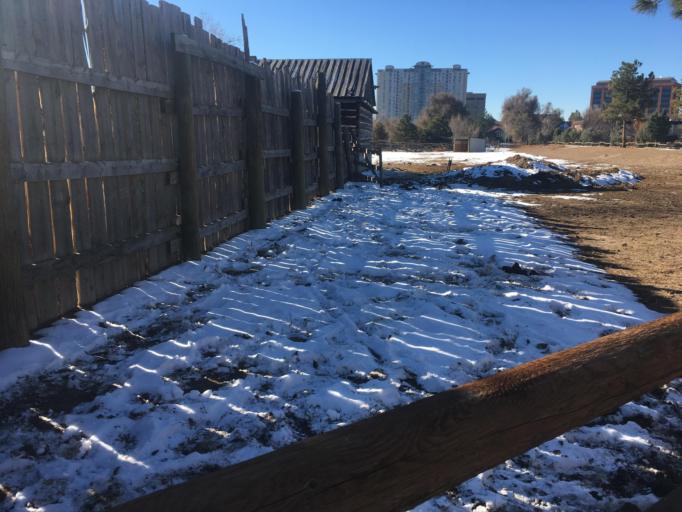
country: US
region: Colorado
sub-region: Arapahoe County
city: Glendale
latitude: 39.7037
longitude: -104.9270
